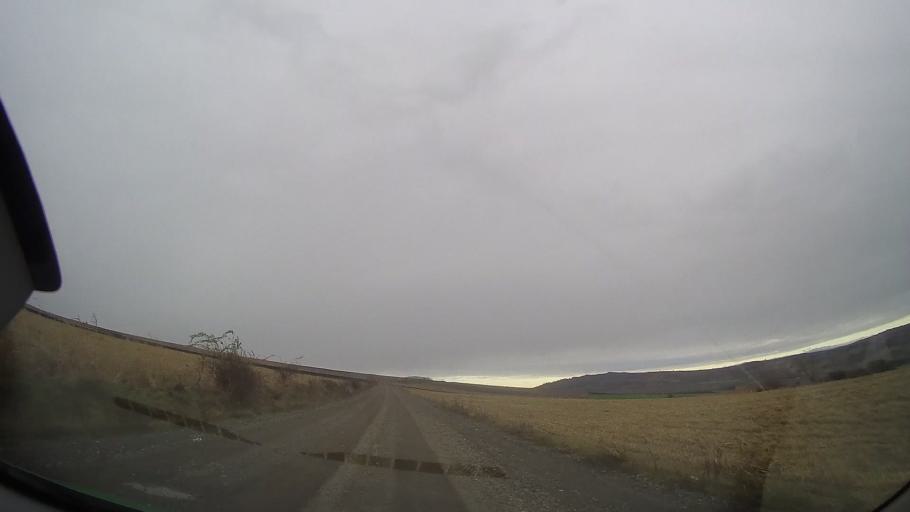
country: RO
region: Mures
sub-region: Comuna Ceausu de Campie
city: Ceausu de Campie
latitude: 46.6613
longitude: 24.4872
